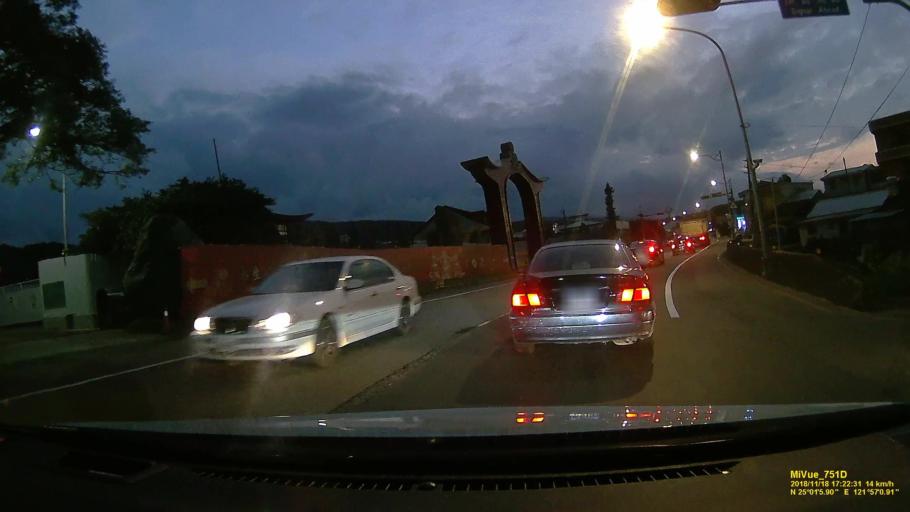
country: TW
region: Taiwan
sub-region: Keelung
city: Keelung
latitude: 25.0183
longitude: 121.9502
